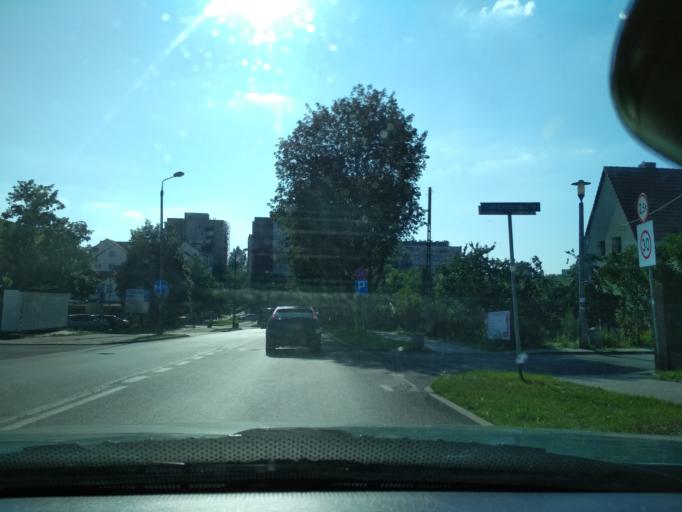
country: PL
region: Silesian Voivodeship
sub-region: Gliwice
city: Gliwice
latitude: 50.2767
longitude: 18.6603
